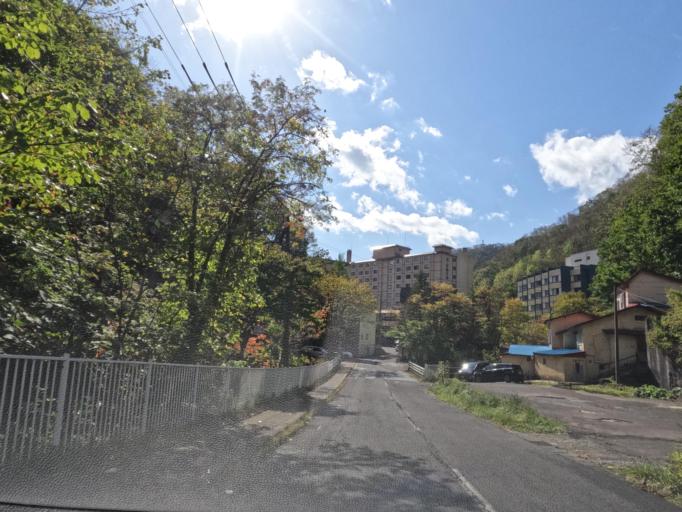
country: JP
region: Hokkaido
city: Shiraoi
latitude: 42.4973
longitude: 141.1414
